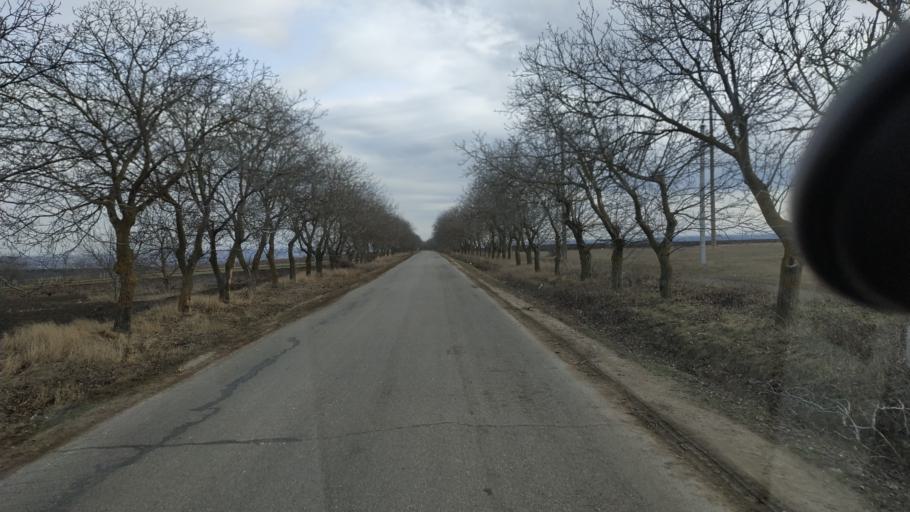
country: MD
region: Telenesti
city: Cocieri
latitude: 47.3003
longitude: 29.0611
